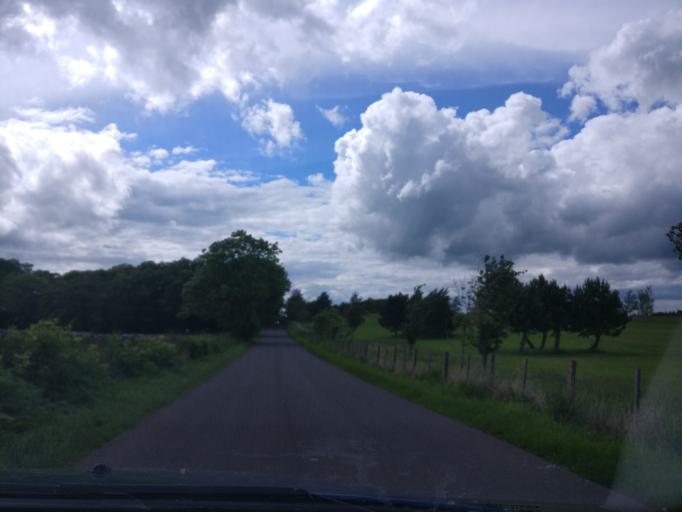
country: GB
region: Scotland
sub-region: East Lothian
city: Haddington
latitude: 55.8843
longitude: -2.7241
